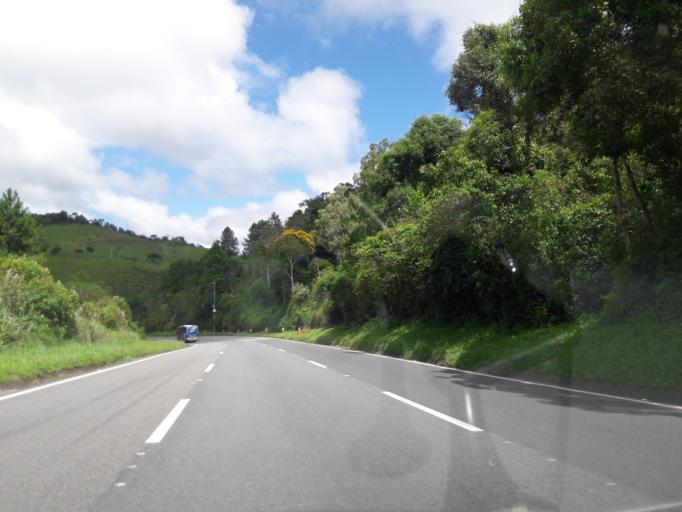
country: BR
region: Sao Paulo
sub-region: Cajati
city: Cajati
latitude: -24.9741
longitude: -48.5038
